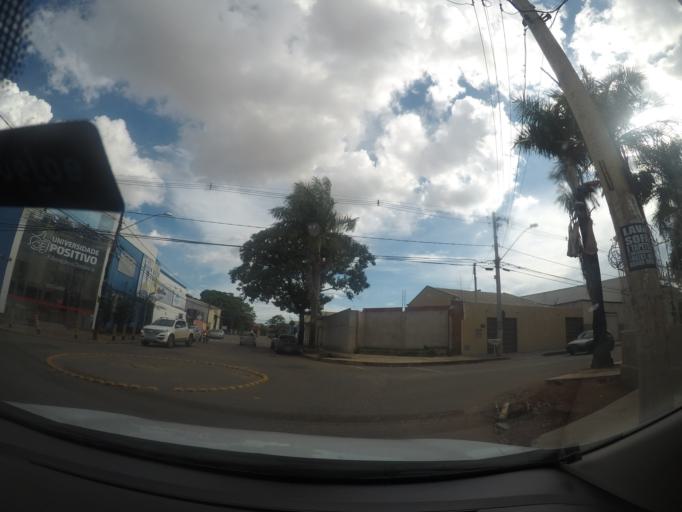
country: BR
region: Goias
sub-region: Goiania
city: Goiania
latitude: -16.6752
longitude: -49.3044
